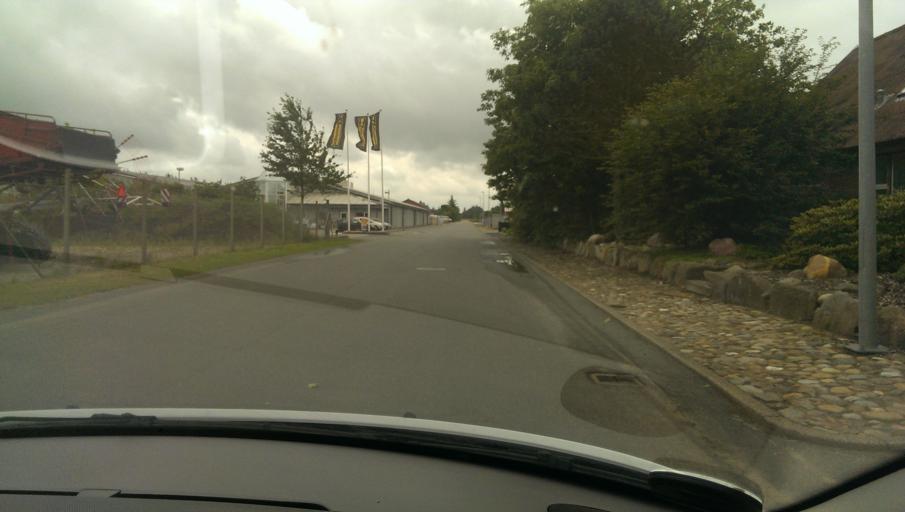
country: DK
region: Central Jutland
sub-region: Holstebro Kommune
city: Ulfborg
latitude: 56.2635
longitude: 8.3220
